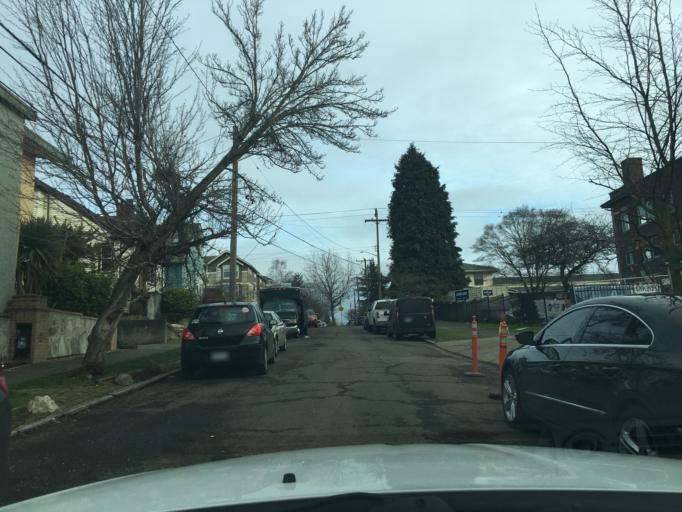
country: US
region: Washington
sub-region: King County
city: Seattle
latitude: 47.6027
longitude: -122.3098
